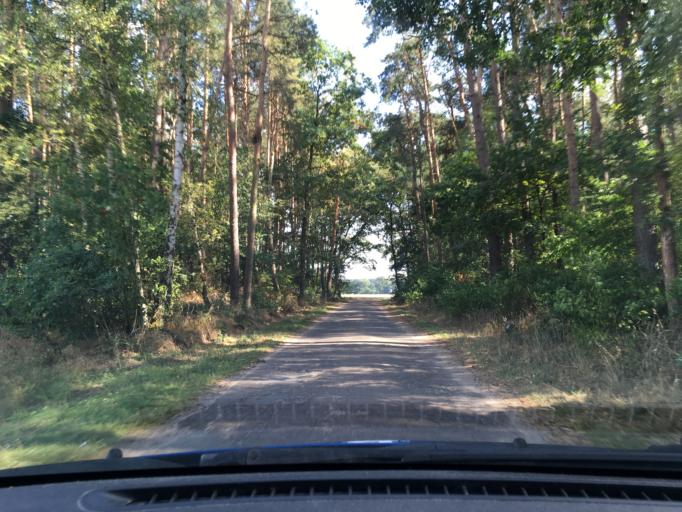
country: DE
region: Lower Saxony
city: Salzhausen
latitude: 53.2156
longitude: 10.2052
